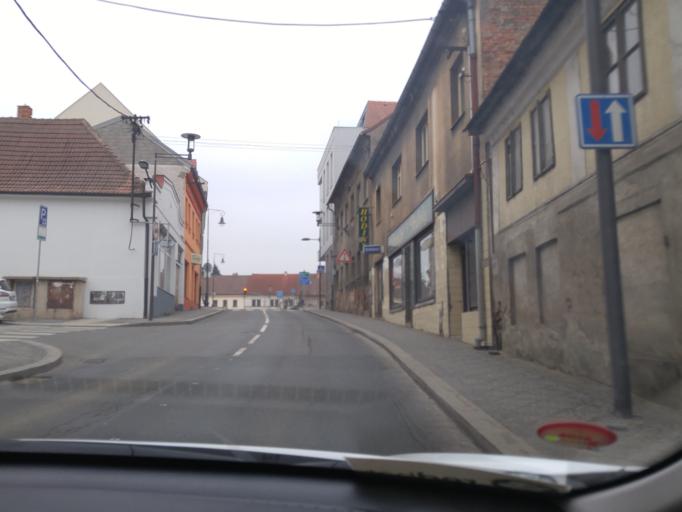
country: CZ
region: Central Bohemia
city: Brandys nad Labem-Stara Boleslav
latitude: 50.1867
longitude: 14.6586
